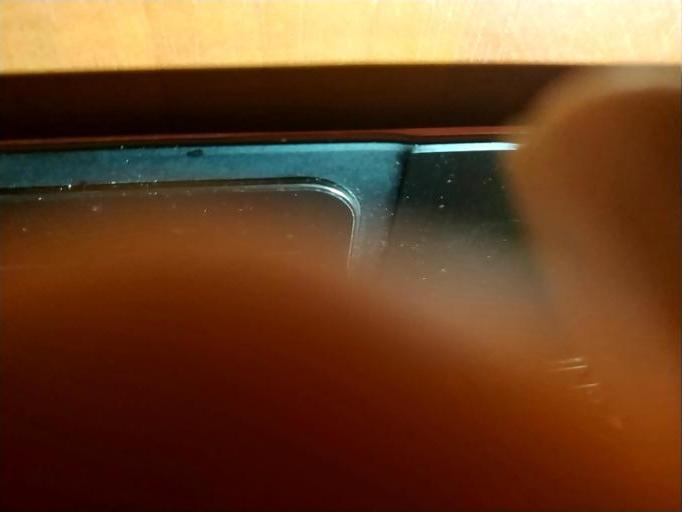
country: RU
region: Tverskaya
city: Ves'yegonsk
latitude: 58.7038
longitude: 37.5439
